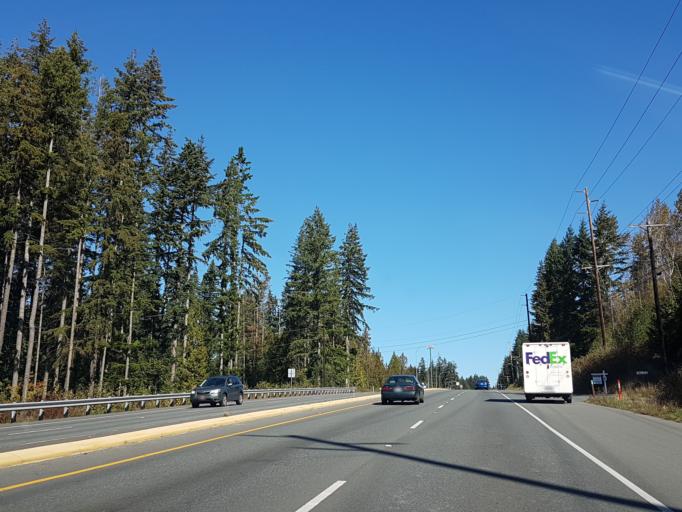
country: US
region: Washington
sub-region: Snohomish County
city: Clearview
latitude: 47.8164
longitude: -122.1392
